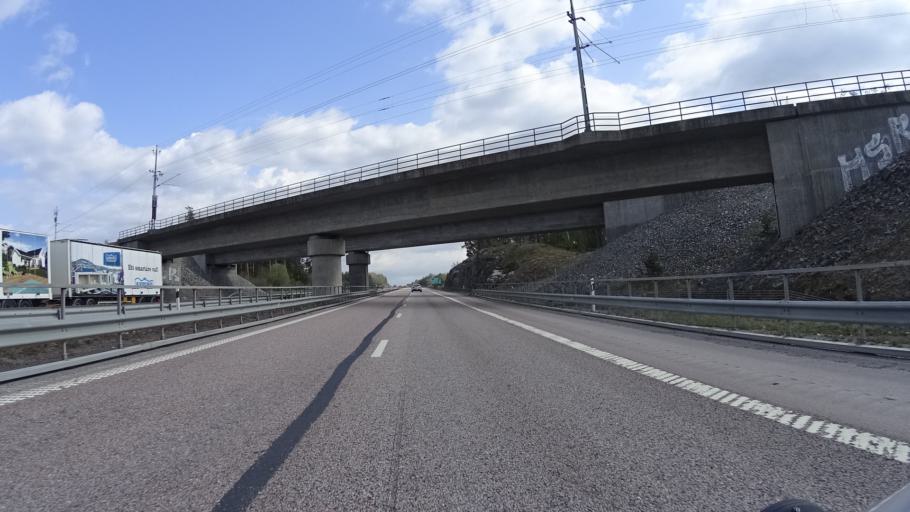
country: SE
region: Soedermanland
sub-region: Strangnas Kommun
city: Strangnas
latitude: 59.3667
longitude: 16.9583
